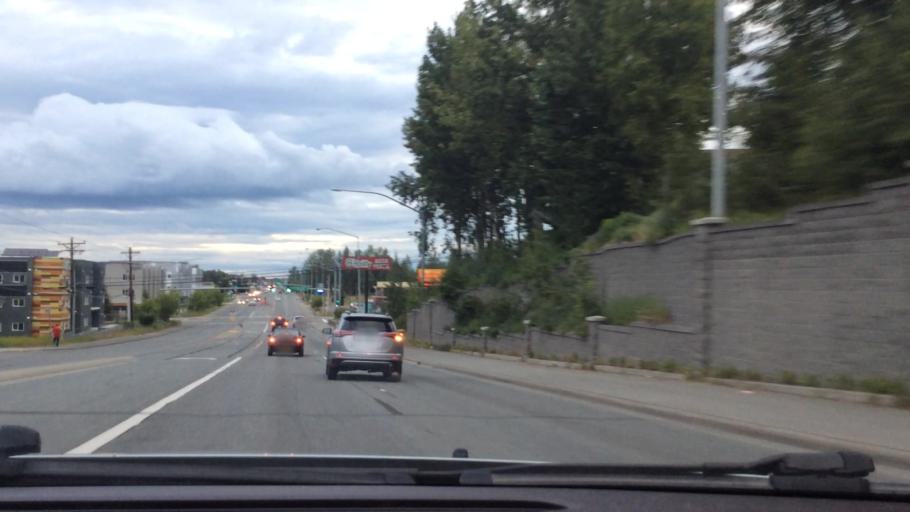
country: US
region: Alaska
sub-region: Anchorage Municipality
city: Elmendorf Air Force Base
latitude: 61.2053
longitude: -149.7333
